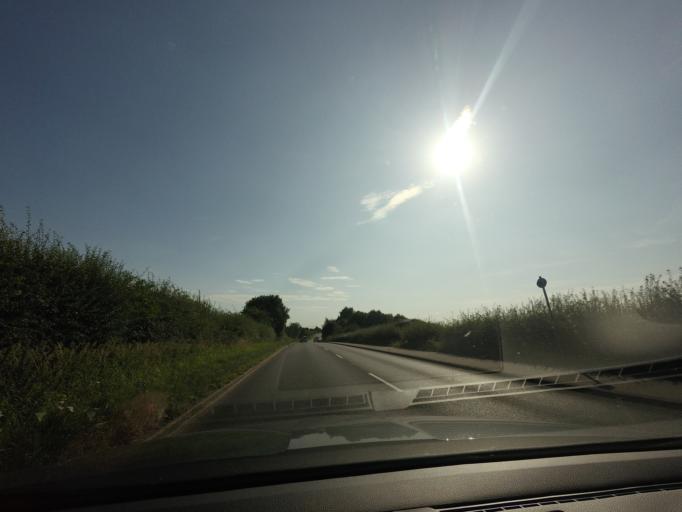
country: GB
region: England
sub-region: Derbyshire
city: Pinxton
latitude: 53.0571
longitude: -1.2850
